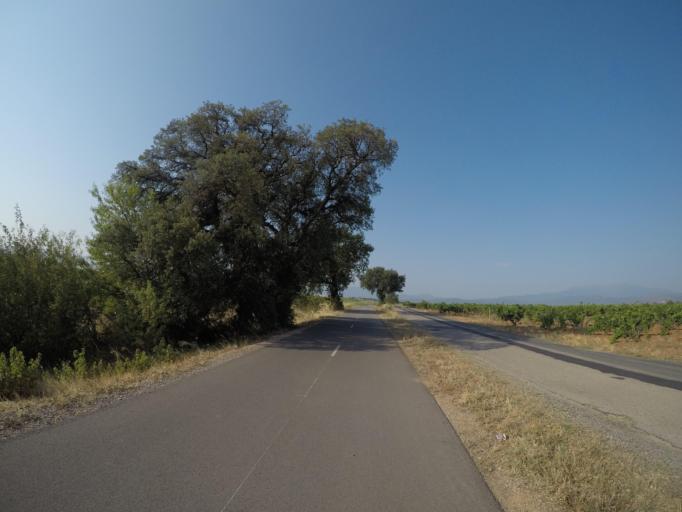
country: FR
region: Languedoc-Roussillon
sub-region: Departement des Pyrenees-Orientales
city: Ponteilla
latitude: 42.6415
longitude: 2.8138
